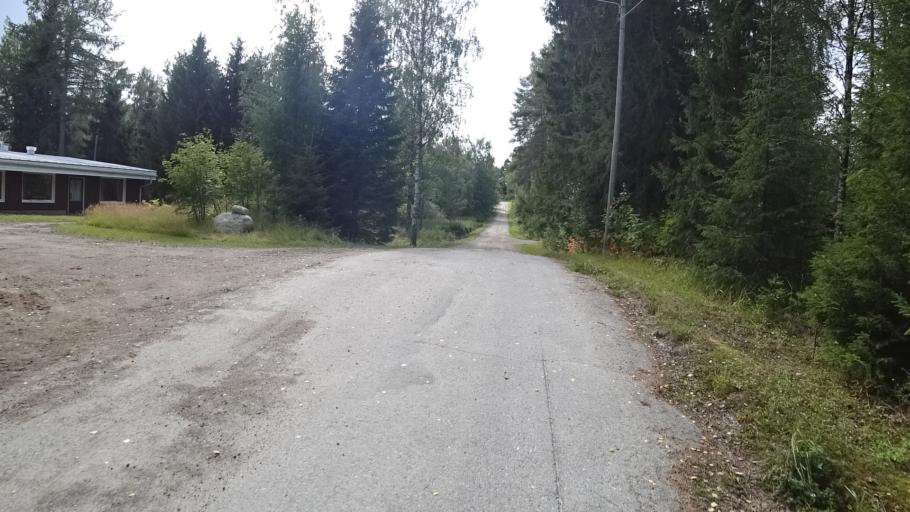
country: FI
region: North Karelia
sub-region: Joensuu
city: Ilomantsi
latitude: 62.6387
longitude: 31.2840
